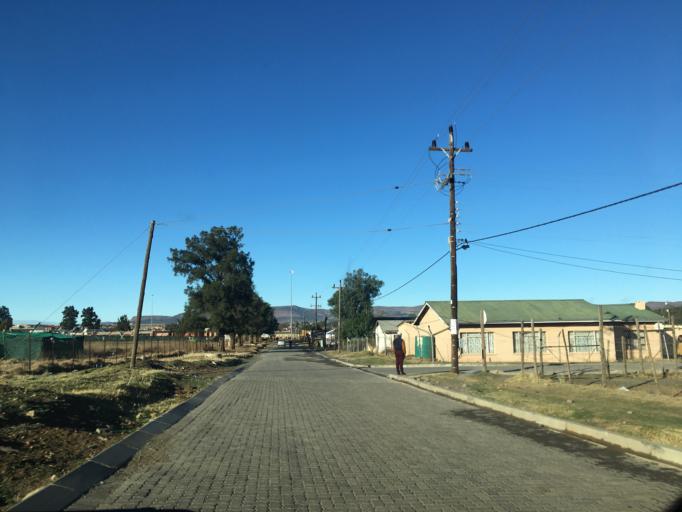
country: ZA
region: Eastern Cape
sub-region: Chris Hani District Municipality
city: Cala
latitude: -31.5285
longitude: 27.6955
